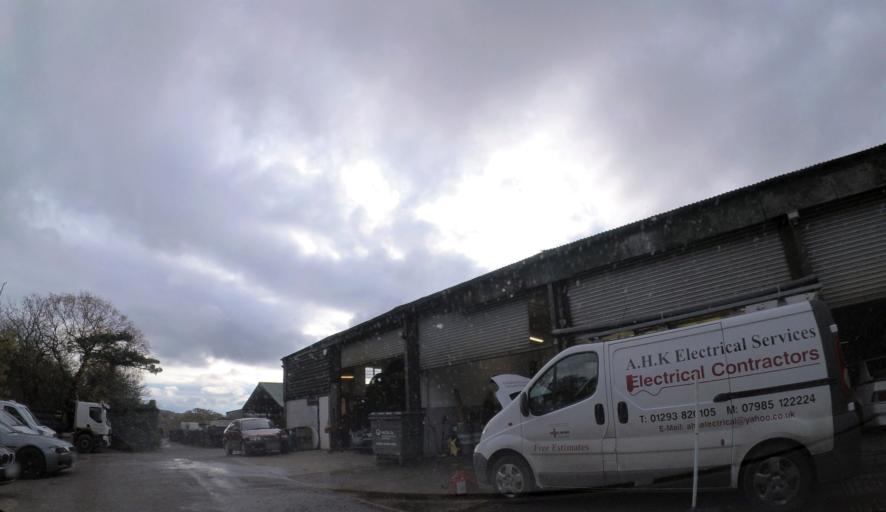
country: GB
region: England
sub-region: Surrey
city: Salfords
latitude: 51.2087
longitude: -0.1715
